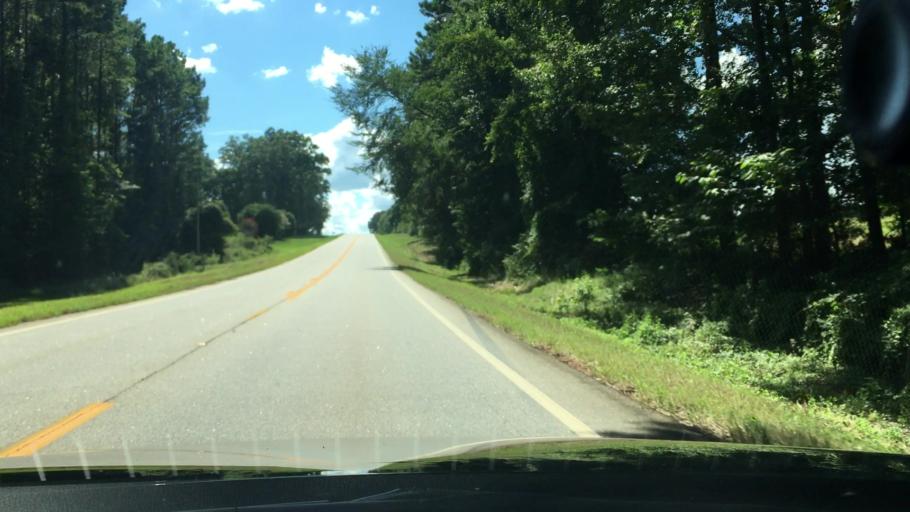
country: US
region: Georgia
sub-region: Jasper County
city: Monticello
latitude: 33.3006
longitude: -83.7144
